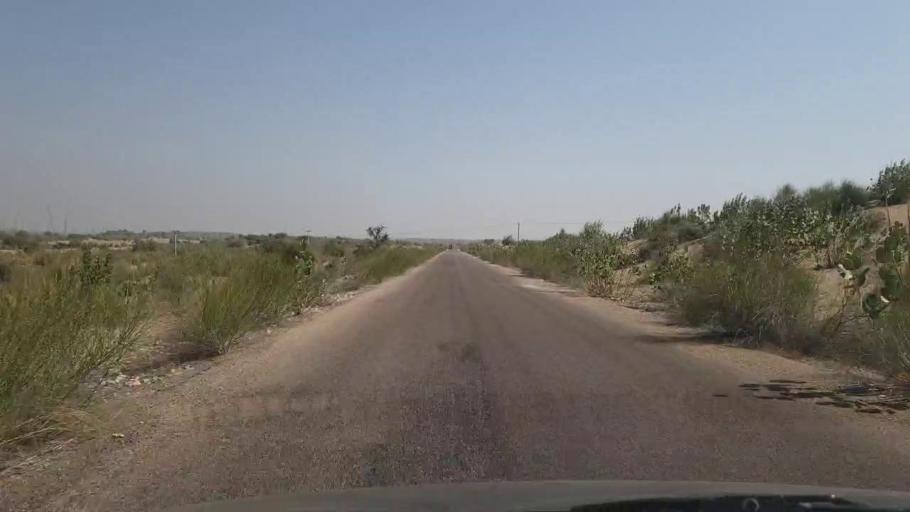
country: PK
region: Sindh
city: Chor
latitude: 25.6015
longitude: 70.0201
